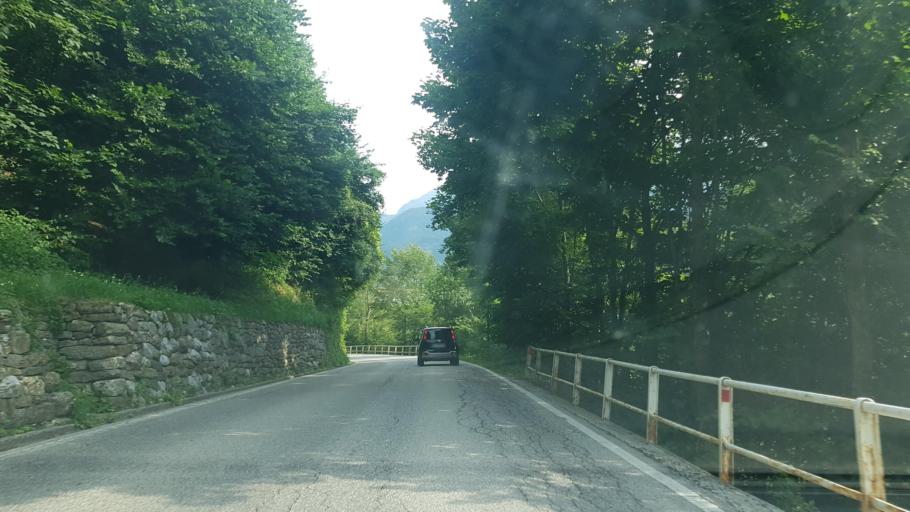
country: IT
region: Friuli Venezia Giulia
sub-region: Provincia di Udine
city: Paularo
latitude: 46.5227
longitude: 13.1218
